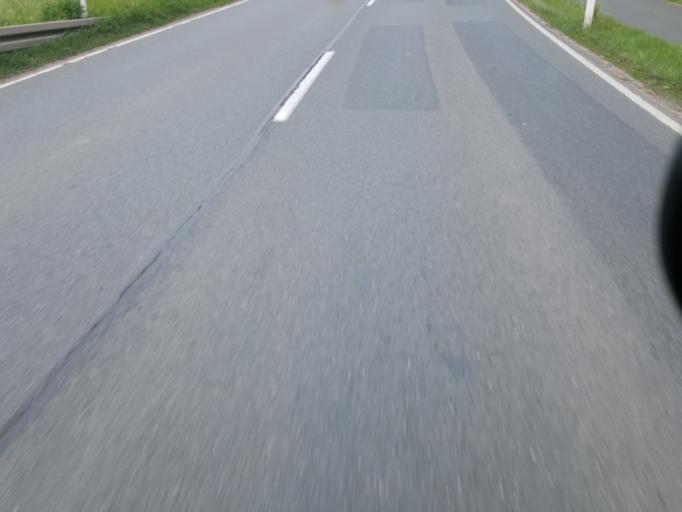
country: DE
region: Lower Saxony
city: Leese
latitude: 52.5079
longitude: 9.1053
